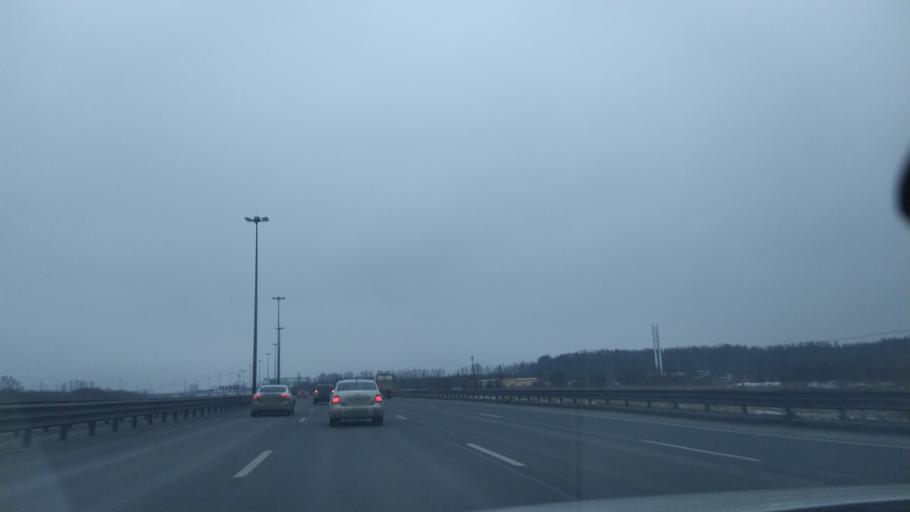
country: RU
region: St.-Petersburg
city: Krasnogvargeisky
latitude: 59.9983
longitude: 30.4766
